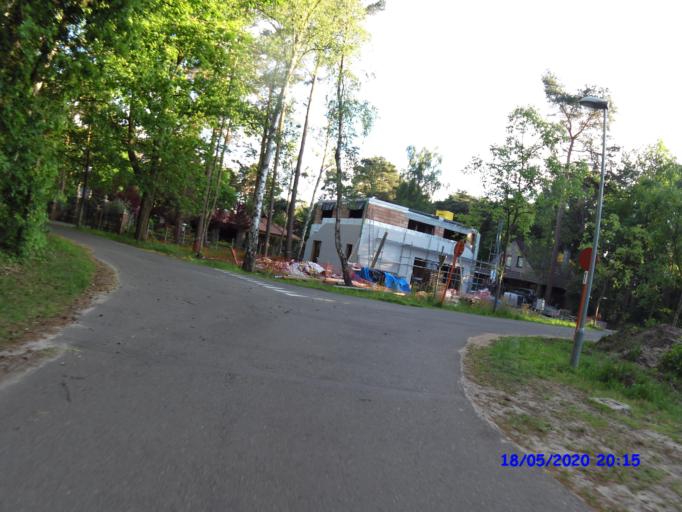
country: BE
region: Flanders
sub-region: Provincie Antwerpen
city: Kasterlee
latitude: 51.2040
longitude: 4.9078
